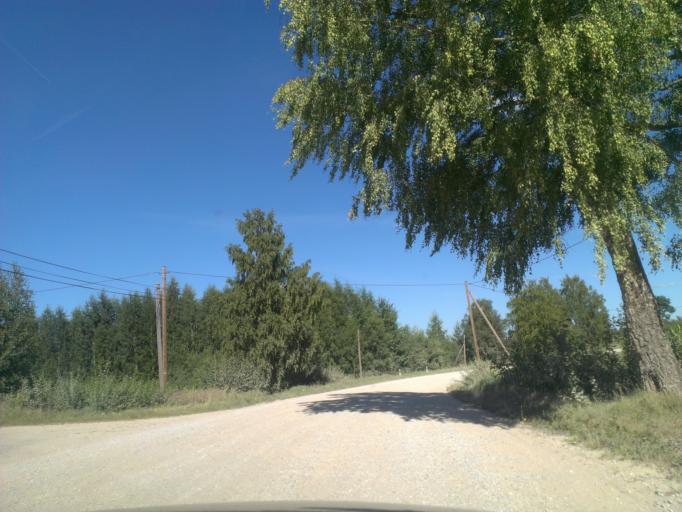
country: LV
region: Malpils
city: Malpils
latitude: 57.0154
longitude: 24.9877
